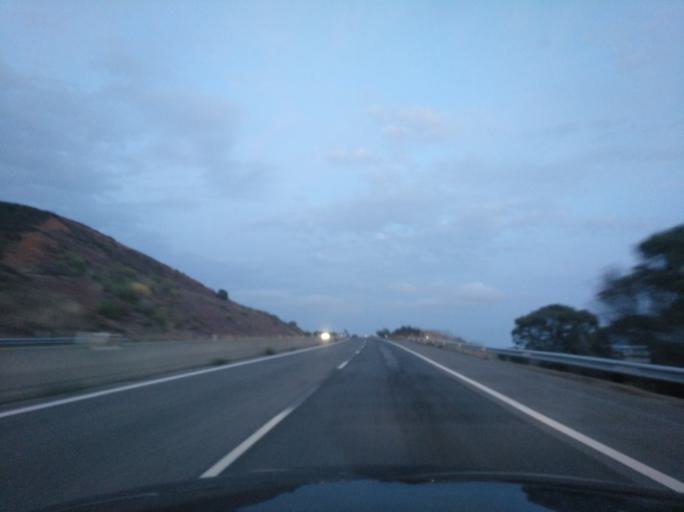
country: PT
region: Faro
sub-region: Lagos
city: Lagos
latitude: 37.1655
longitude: -8.6742
